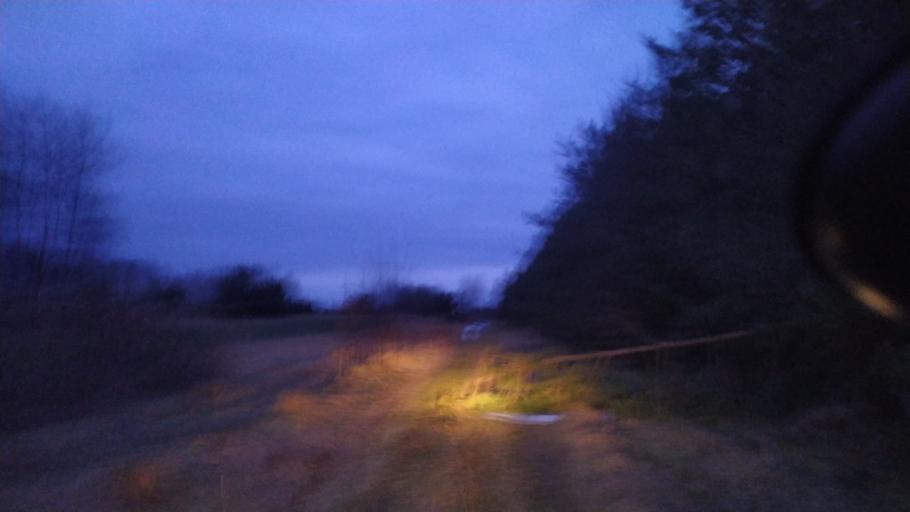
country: PL
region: Lublin Voivodeship
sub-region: Powiat lubelski
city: Jastkow
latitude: 51.3848
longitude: 22.4366
